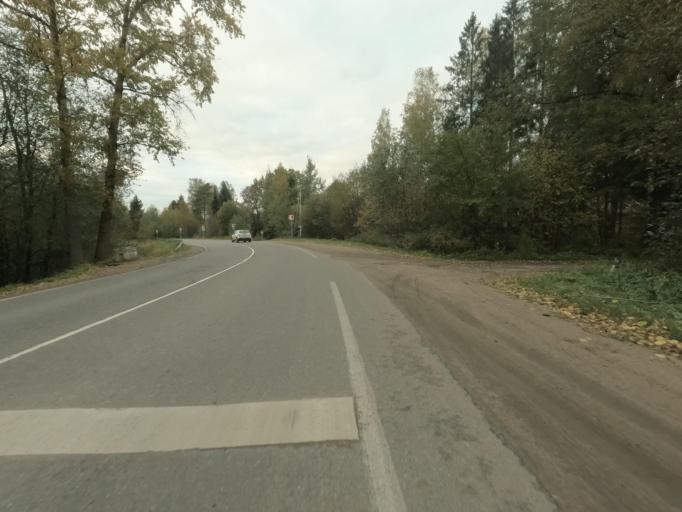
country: RU
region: Leningrad
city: Pavlovo
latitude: 59.7857
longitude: 30.9696
